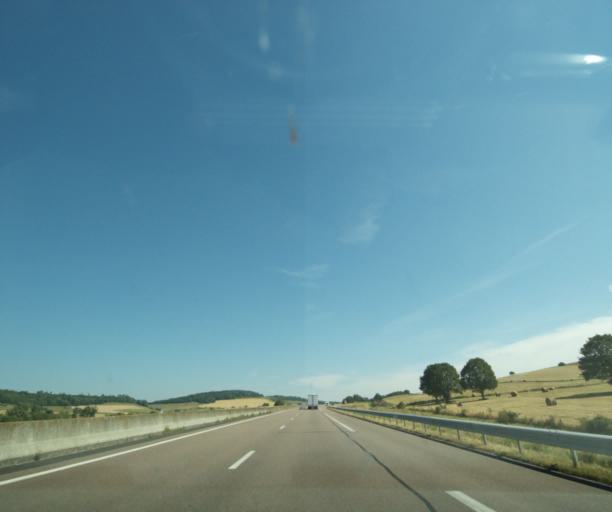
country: FR
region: Lorraine
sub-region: Departement des Vosges
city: Chatenois
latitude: 48.3612
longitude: 5.8666
